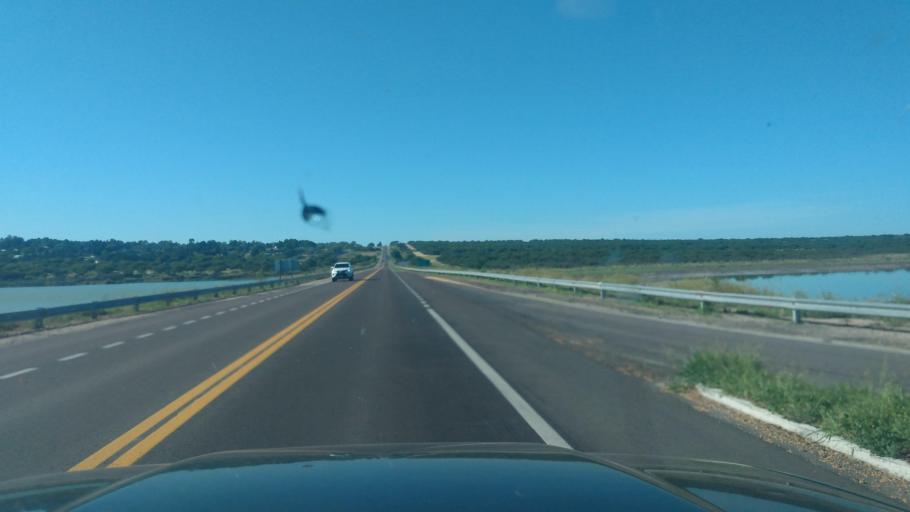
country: AR
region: La Pampa
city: Santa Rosa
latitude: -36.7160
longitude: -64.2831
